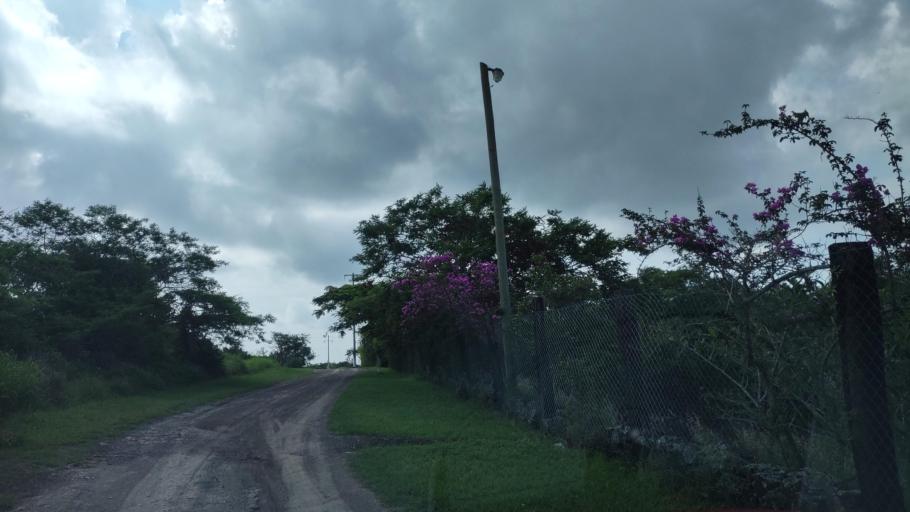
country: MX
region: Veracruz
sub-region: Emiliano Zapata
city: Dos Rios
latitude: 19.4512
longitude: -96.8106
